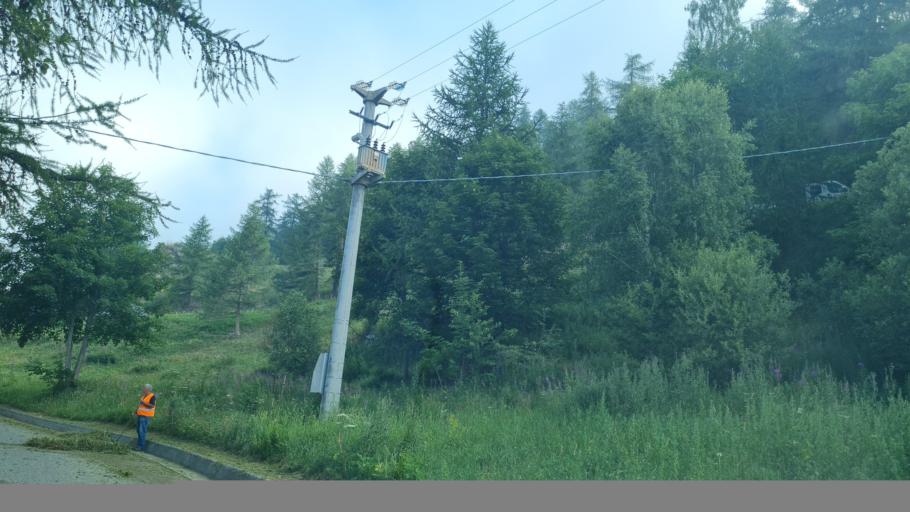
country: IT
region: Aosta Valley
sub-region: Valle d'Aosta
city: La Magdeleine
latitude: 45.8158
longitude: 7.6054
